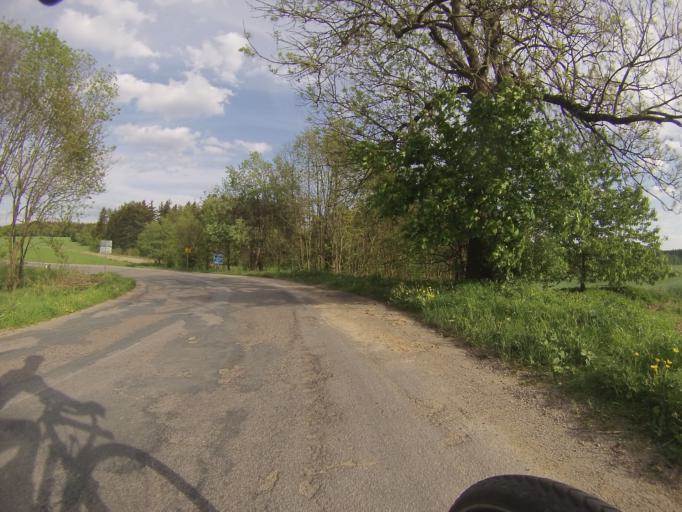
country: CZ
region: Olomoucky
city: Protivanov
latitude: 49.4363
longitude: 16.8289
